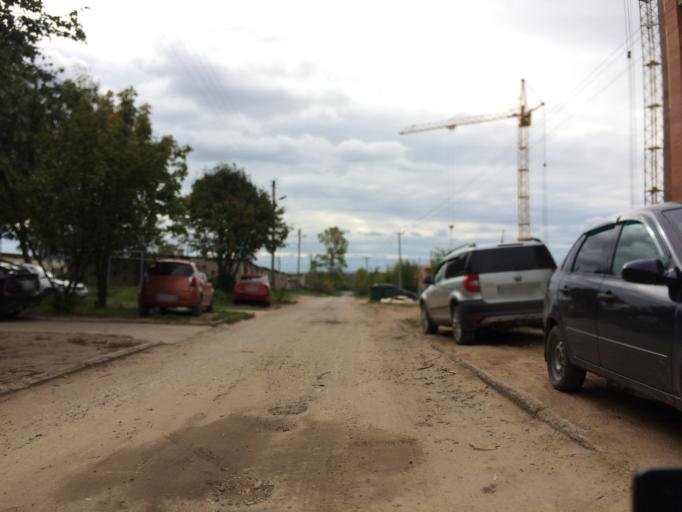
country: RU
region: Mariy-El
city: Yoshkar-Ola
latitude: 56.6534
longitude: 47.9692
